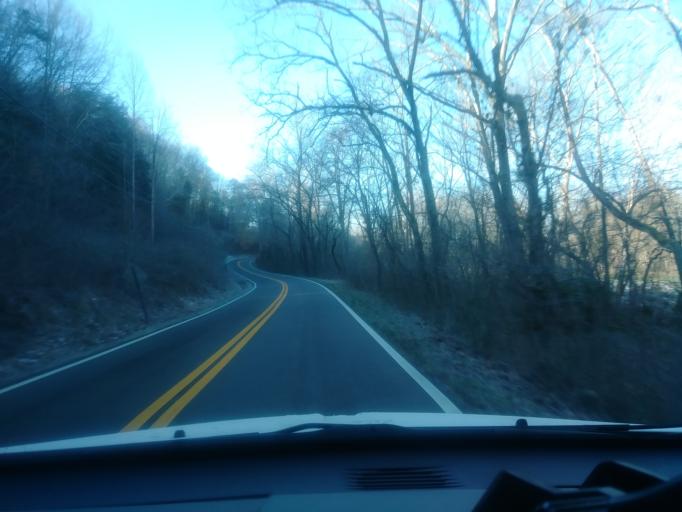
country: US
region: Tennessee
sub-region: Greene County
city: Mosheim
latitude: 36.1222
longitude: -83.0116
